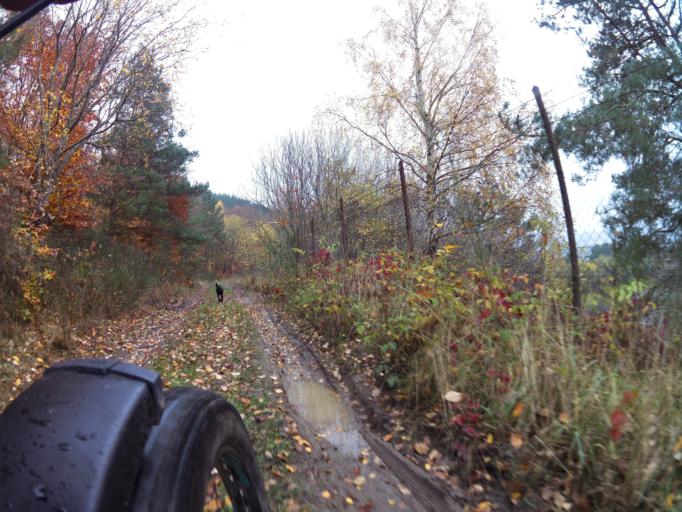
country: PL
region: Pomeranian Voivodeship
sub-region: Powiat wejherowski
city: Gniewino
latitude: 54.7531
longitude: 18.0848
